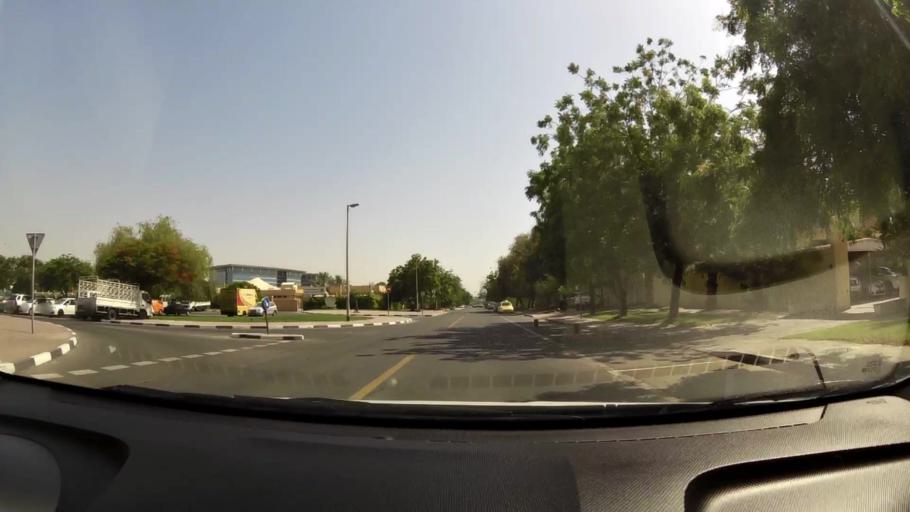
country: AE
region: Ash Shariqah
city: Sharjah
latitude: 25.2662
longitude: 55.3721
